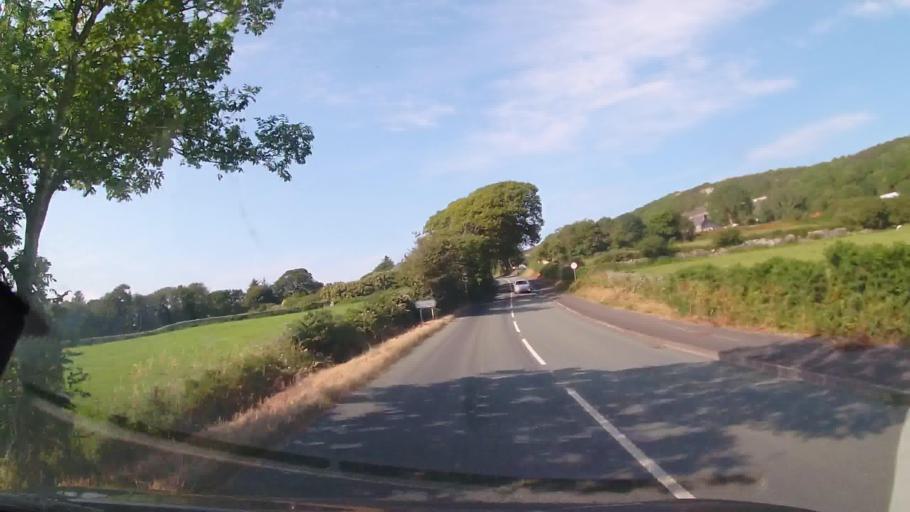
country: GB
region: Wales
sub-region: Gwynedd
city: Llanfair
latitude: 52.8355
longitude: -4.1138
